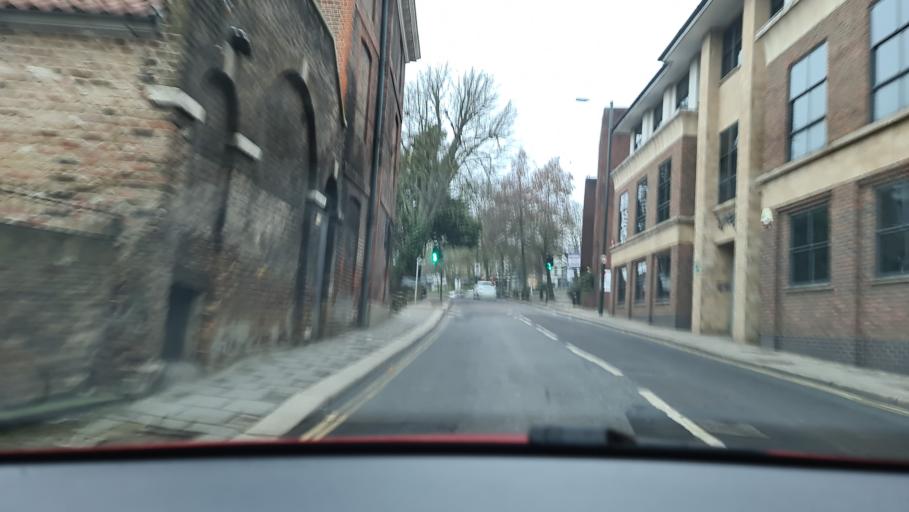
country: GB
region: England
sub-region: Greater London
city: Richmond
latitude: 51.4559
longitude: -0.3035
